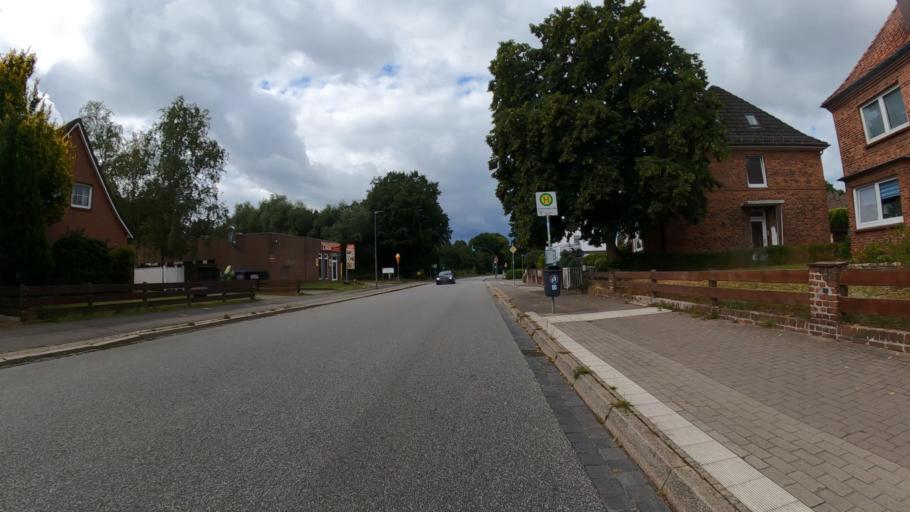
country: DE
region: Schleswig-Holstein
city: Neumunster
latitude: 54.0654
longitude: 9.9677
